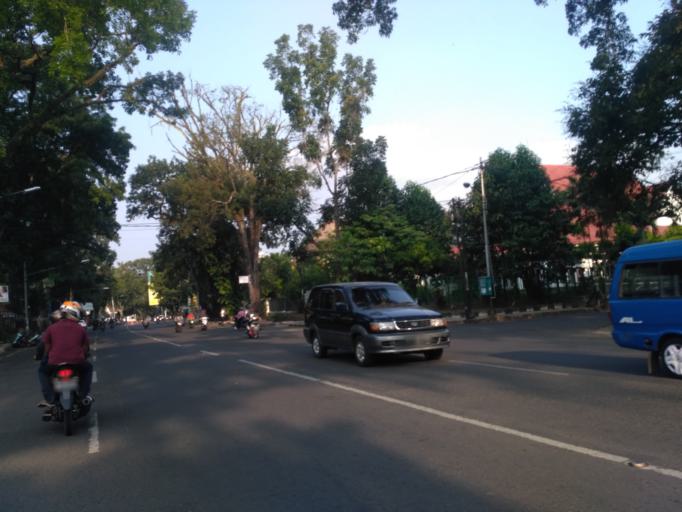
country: ID
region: East Java
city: Malang
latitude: -7.9727
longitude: 112.6226
